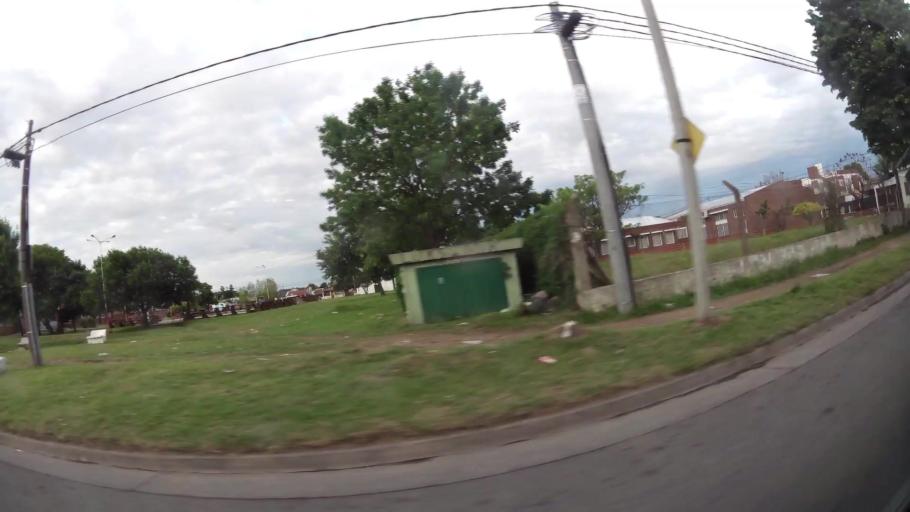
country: AR
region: Buenos Aires
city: San Nicolas de los Arroyos
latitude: -33.3301
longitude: -60.2312
